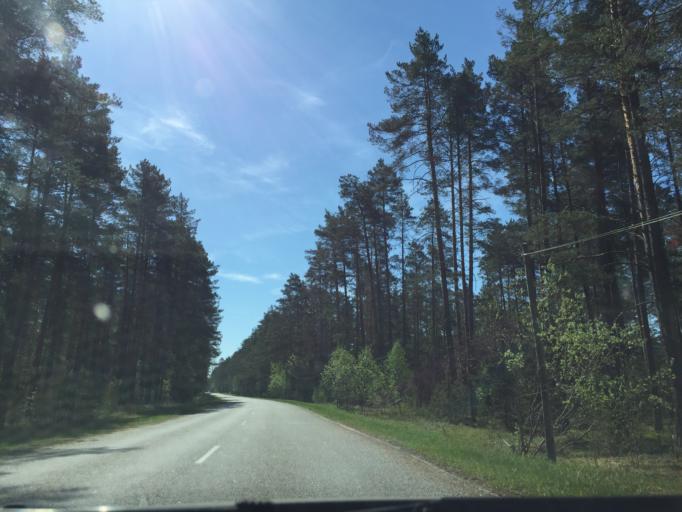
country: LV
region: Garkalne
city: Garkalne
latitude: 57.0249
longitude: 24.4321
